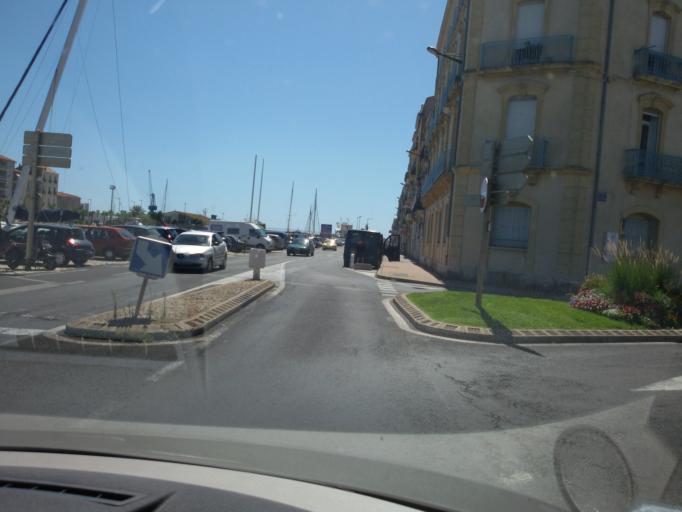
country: FR
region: Languedoc-Roussillon
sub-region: Departement de l'Herault
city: Sete
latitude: 43.4073
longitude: 3.7009
